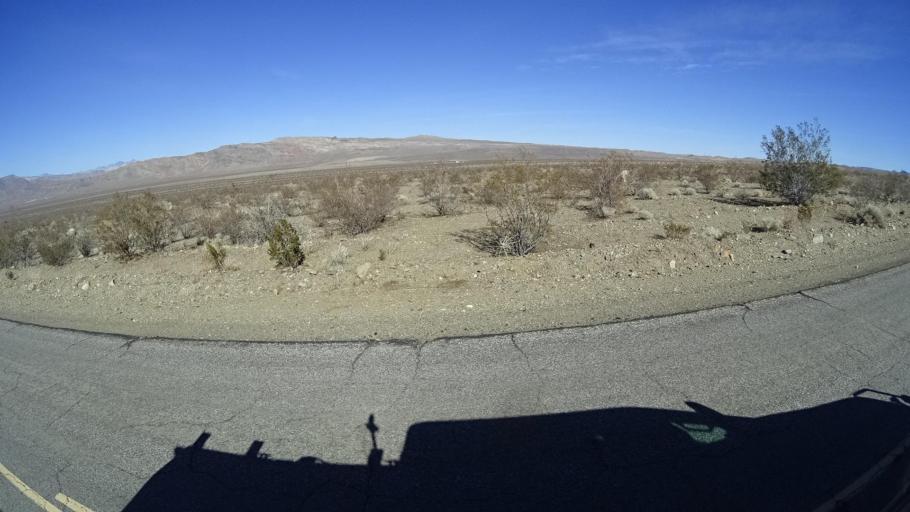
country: US
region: California
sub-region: Kern County
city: Ridgecrest
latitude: 35.3819
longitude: -117.6905
